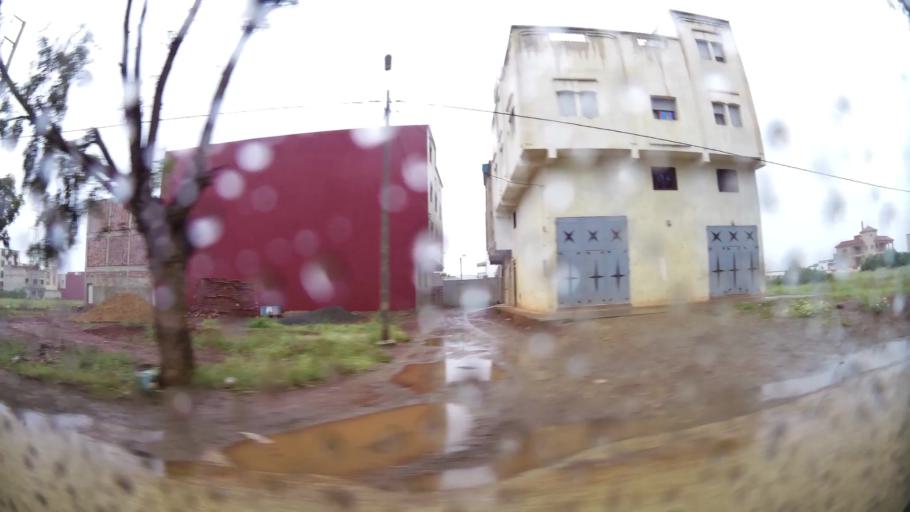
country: MA
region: Oriental
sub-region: Nador
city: Boudinar
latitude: 35.1237
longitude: -3.6464
